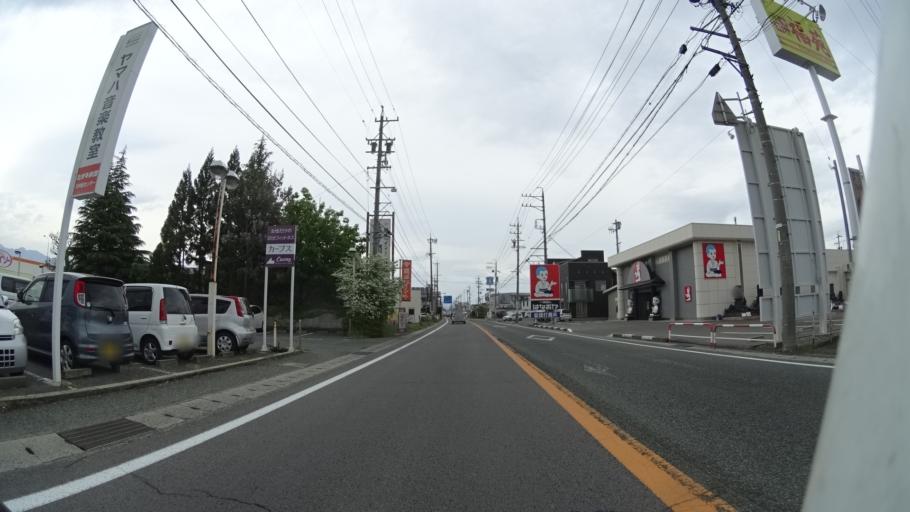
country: JP
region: Nagano
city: Nagano-shi
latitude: 36.5864
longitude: 138.1520
